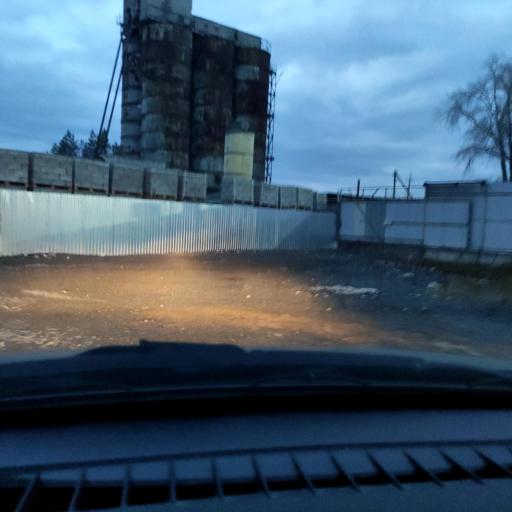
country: RU
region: Samara
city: Zhigulevsk
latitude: 53.4675
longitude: 49.5545
